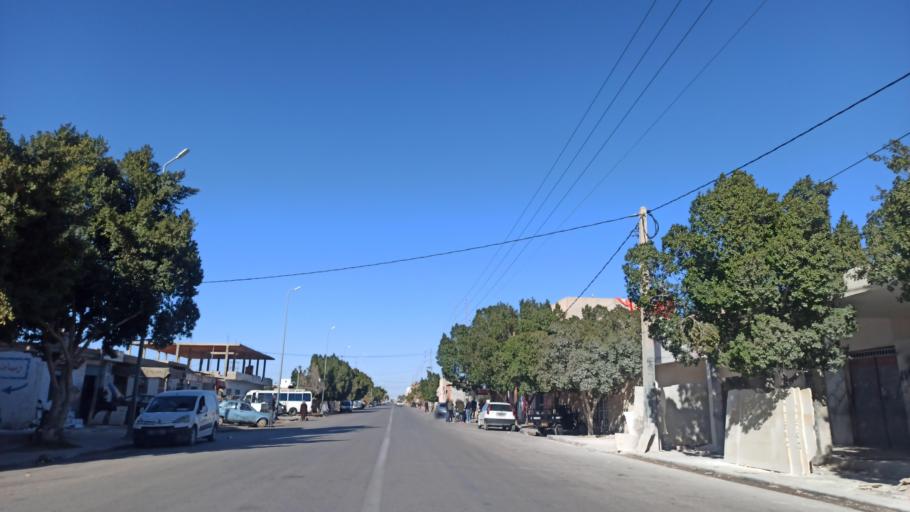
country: TN
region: Sidi Bu Zayd
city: Jilma
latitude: 35.2734
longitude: 9.4190
